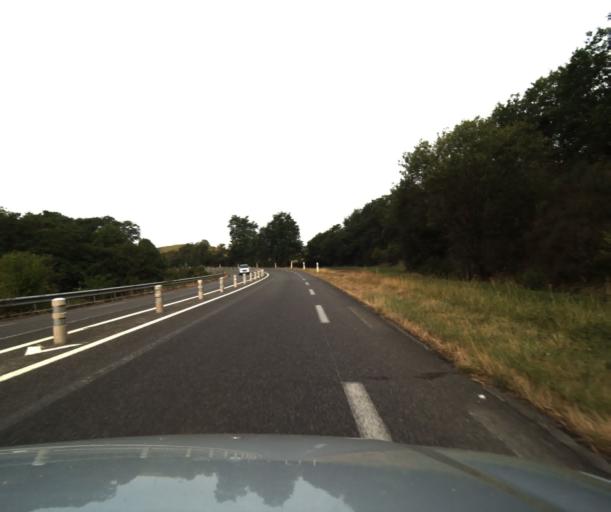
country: FR
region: Midi-Pyrenees
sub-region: Departement du Gers
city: Mirande
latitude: 43.5519
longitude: 0.4925
